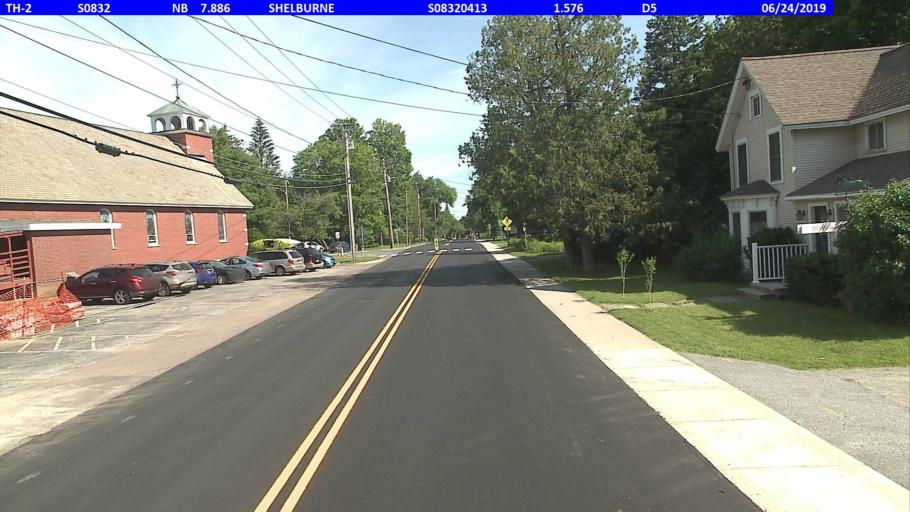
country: US
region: Vermont
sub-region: Chittenden County
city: Burlington
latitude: 44.3772
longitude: -73.2264
